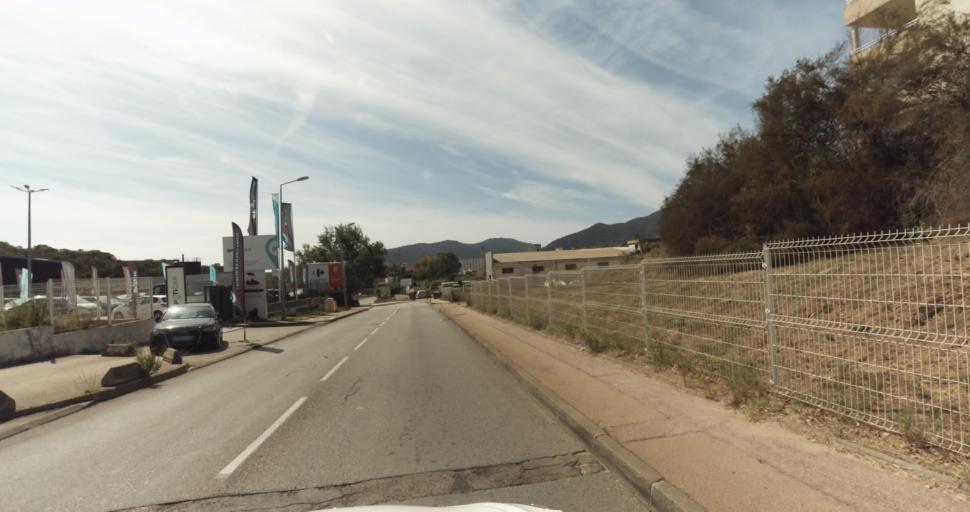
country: FR
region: Corsica
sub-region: Departement de la Corse-du-Sud
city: Ajaccio
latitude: 41.9470
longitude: 8.7621
